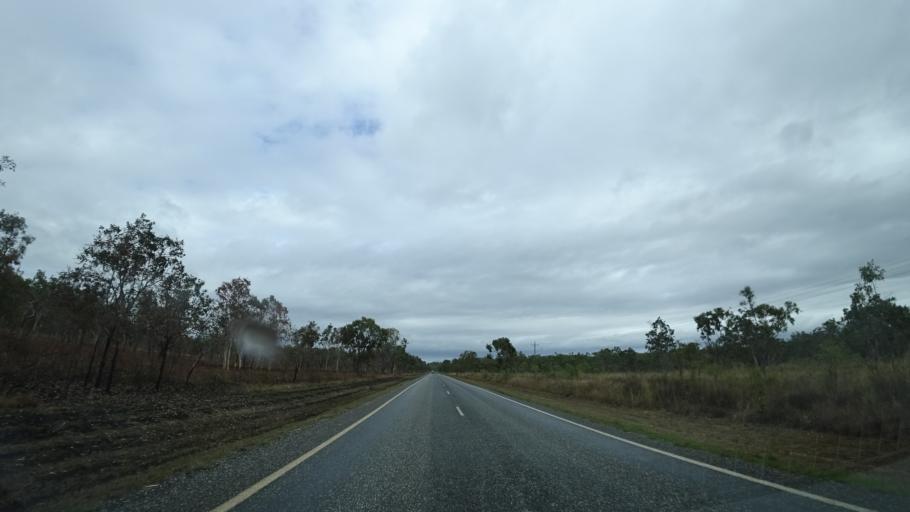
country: AU
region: Queensland
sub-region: Tablelands
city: Mareeba
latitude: -16.7611
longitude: 145.3418
